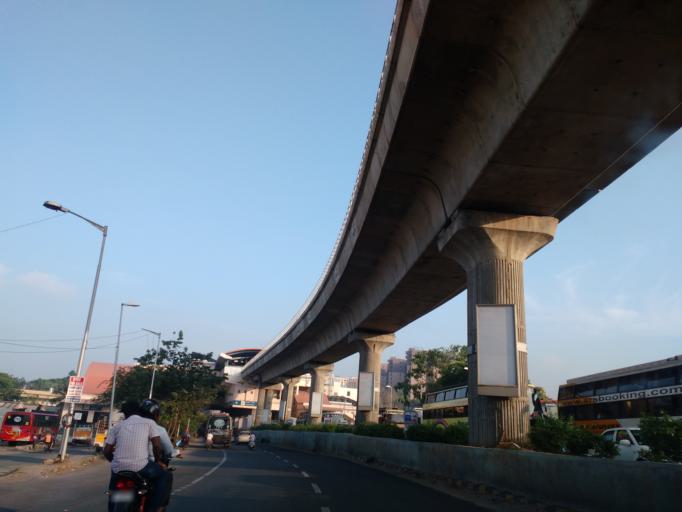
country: IN
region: Karnataka
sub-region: Bangalore Urban
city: Bangalore
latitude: 13.0219
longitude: 77.5518
